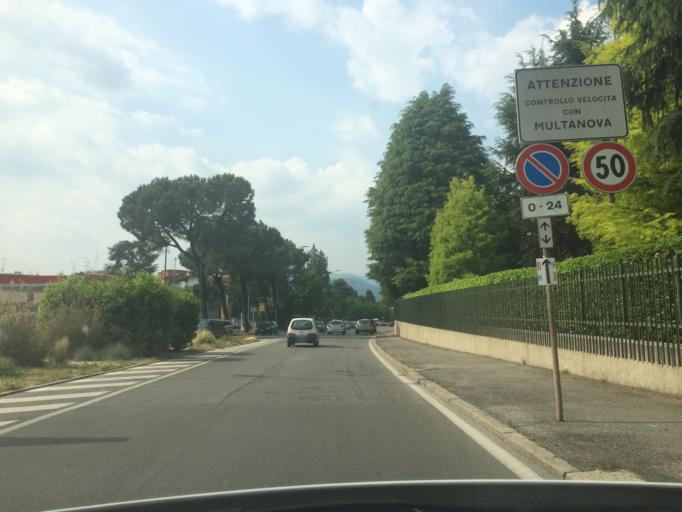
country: IT
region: Lombardy
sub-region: Provincia di Brescia
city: Brescia
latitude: 45.5437
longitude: 10.2308
